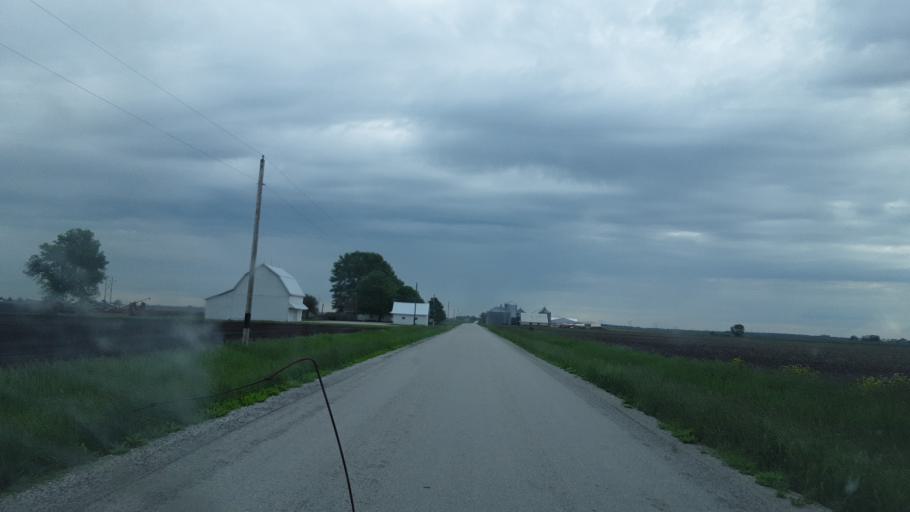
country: US
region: Illinois
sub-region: McDonough County
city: Macomb
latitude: 40.3814
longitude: -90.5331
